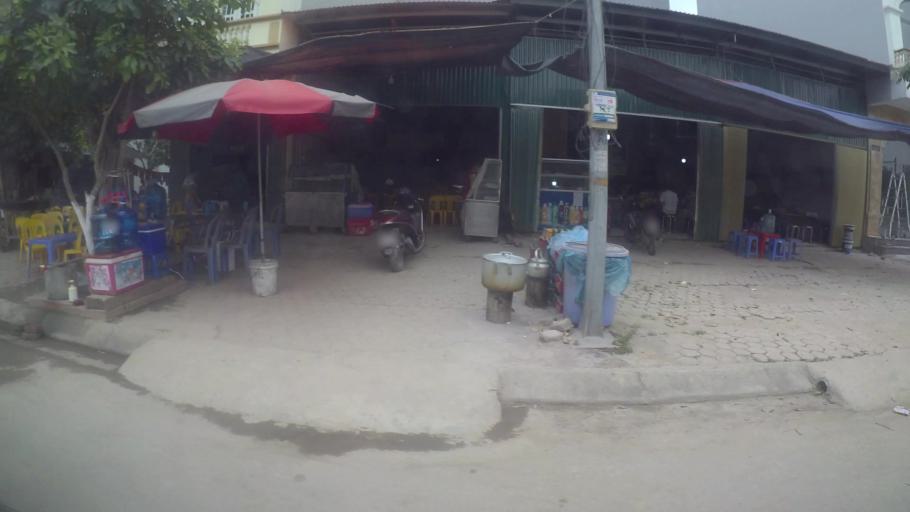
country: VN
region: Ha Noi
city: Ha Dong
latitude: 20.9872
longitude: 105.7508
